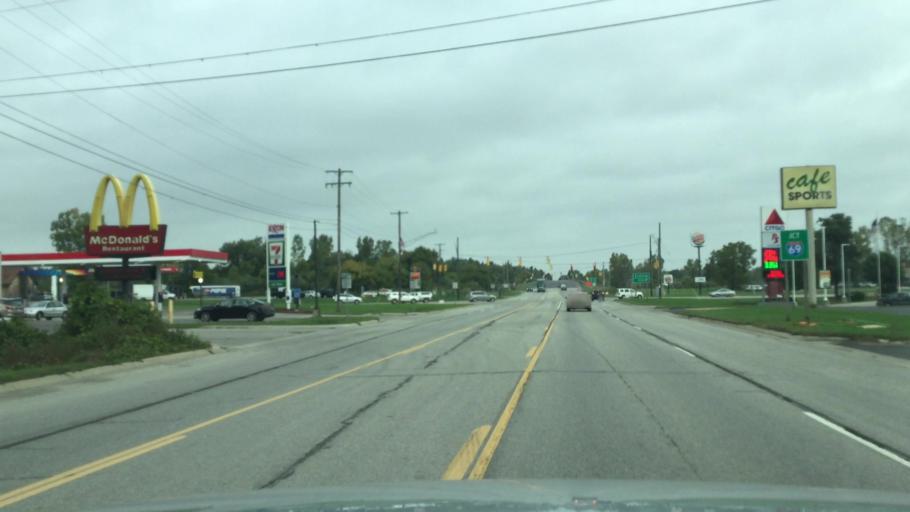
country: US
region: Michigan
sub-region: Shiawassee County
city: Perry
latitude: 42.8345
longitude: -84.2195
